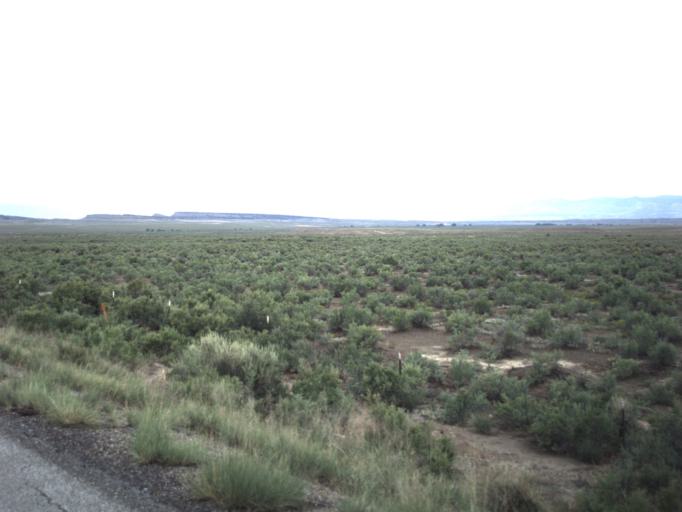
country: US
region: Utah
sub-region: Carbon County
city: East Carbon City
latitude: 39.5322
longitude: -110.5431
